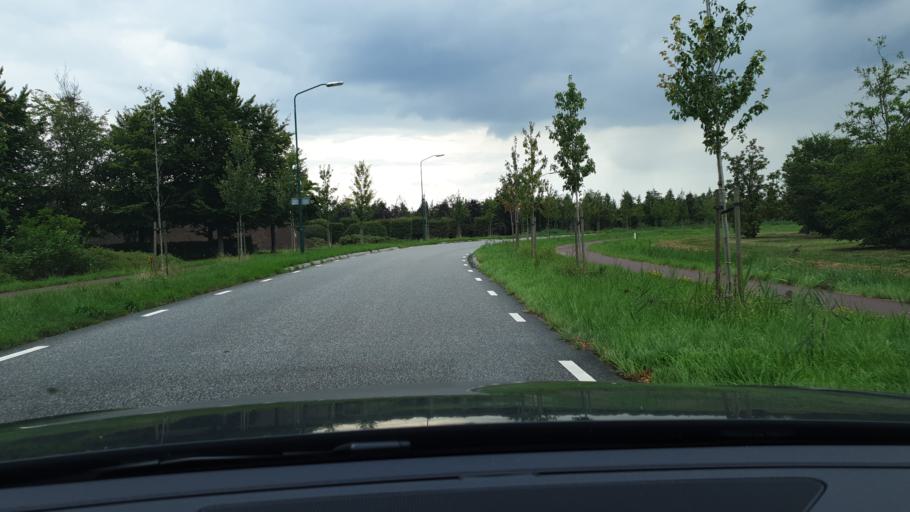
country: NL
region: North Brabant
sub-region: Gemeente Best
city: Best
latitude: 51.5408
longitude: 5.4164
